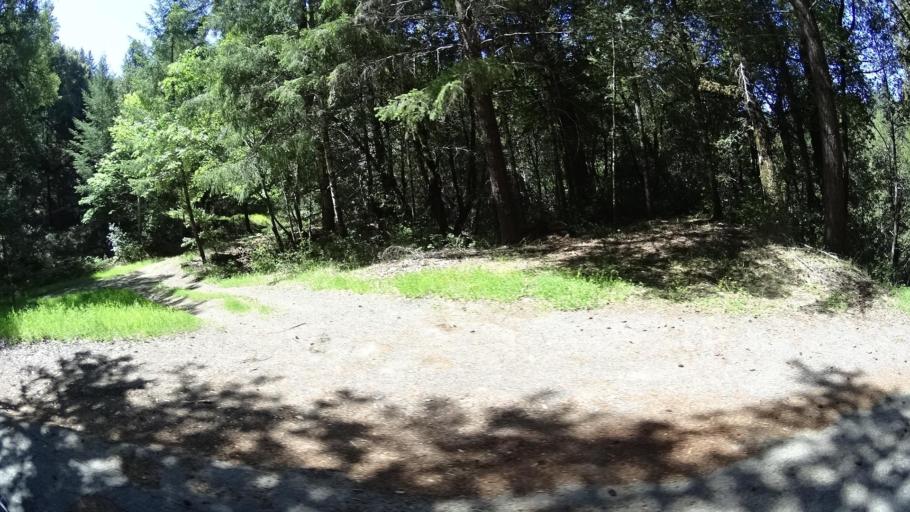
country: US
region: California
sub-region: Humboldt County
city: Redway
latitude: 40.1389
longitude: -123.9895
